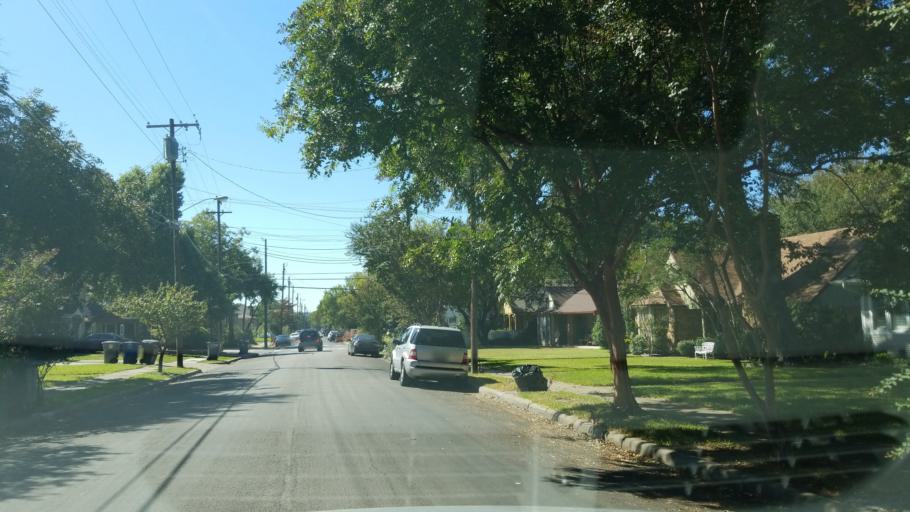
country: US
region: Texas
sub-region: Dallas County
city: Highland Park
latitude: 32.8026
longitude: -96.7568
